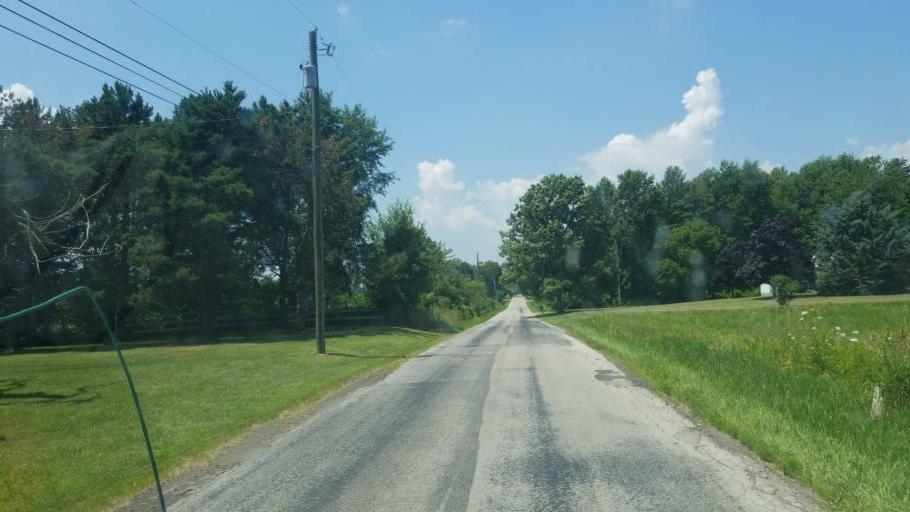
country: US
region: Ohio
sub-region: Richland County
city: Ontario
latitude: 40.8285
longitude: -82.5627
